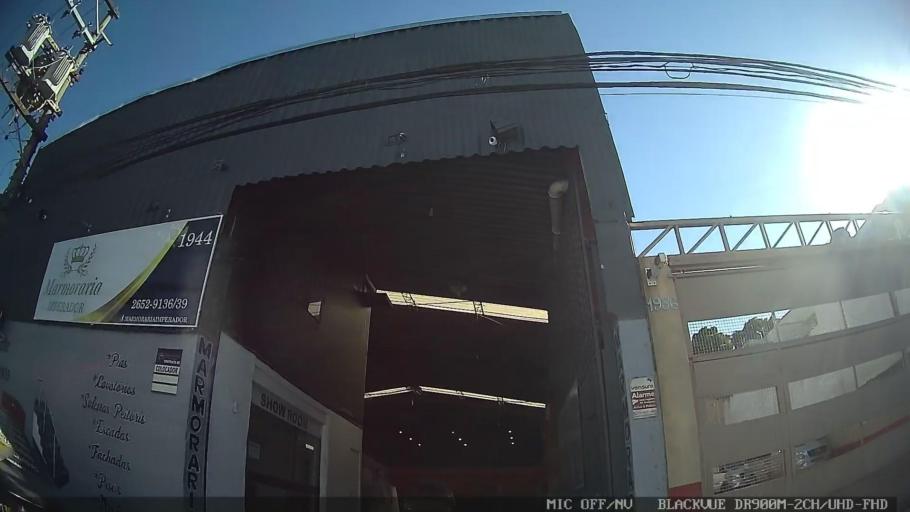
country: BR
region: Sao Paulo
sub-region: Guarulhos
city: Guarulhos
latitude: -23.5409
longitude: -46.5153
